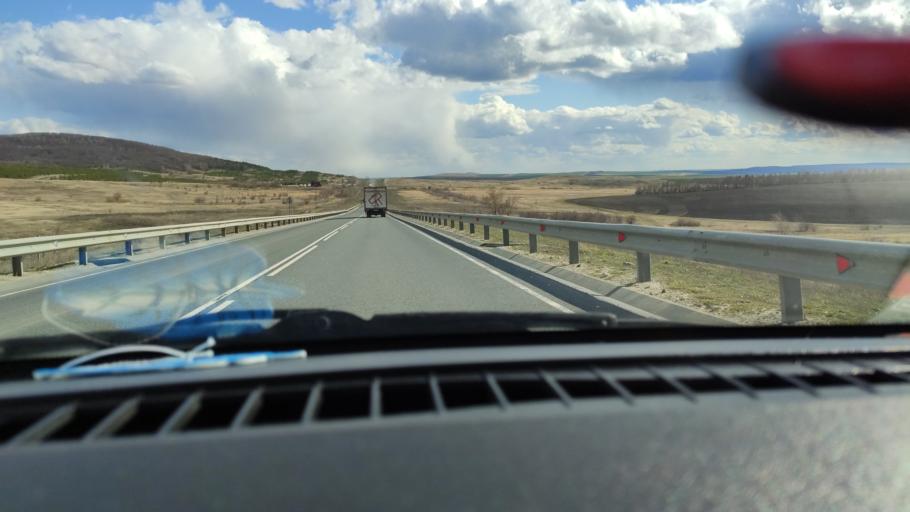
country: RU
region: Saratov
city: Alekseyevka
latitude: 52.3122
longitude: 47.9241
